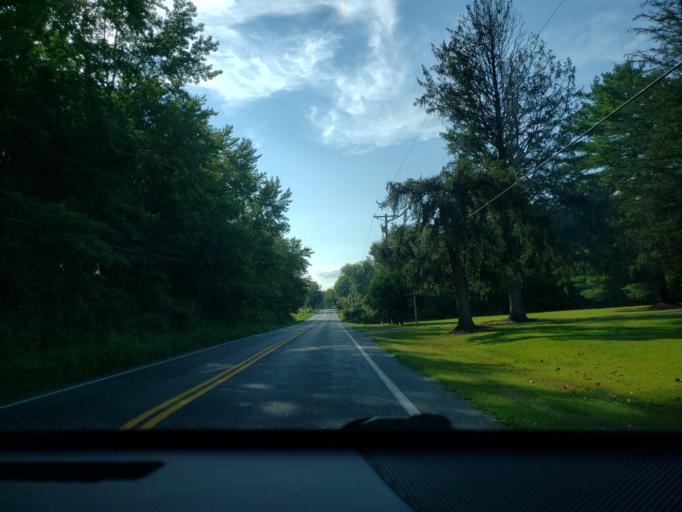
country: US
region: Delaware
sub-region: Sussex County
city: Milton
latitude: 38.7701
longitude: -75.2953
